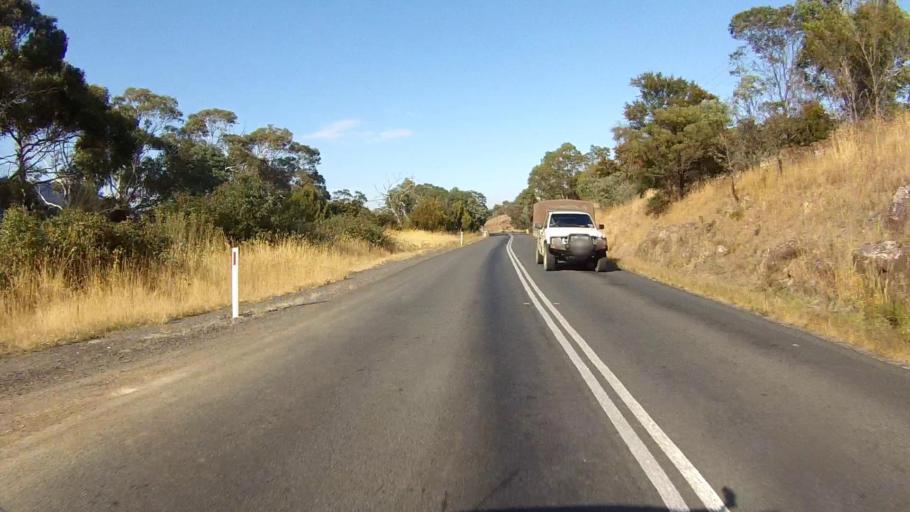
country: AU
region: Tasmania
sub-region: Glenorchy
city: Granton
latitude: -42.7568
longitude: 147.1419
